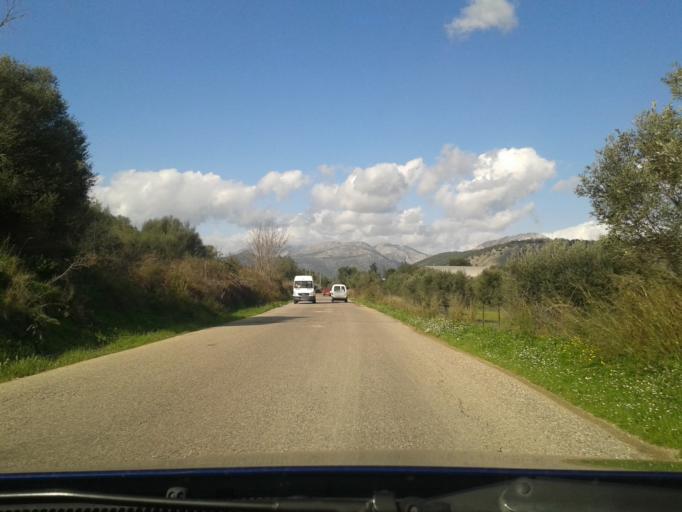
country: GR
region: West Greece
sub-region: Nomos Aitolias kai Akarnanias
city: Astakos
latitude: 38.5590
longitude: 21.0978
